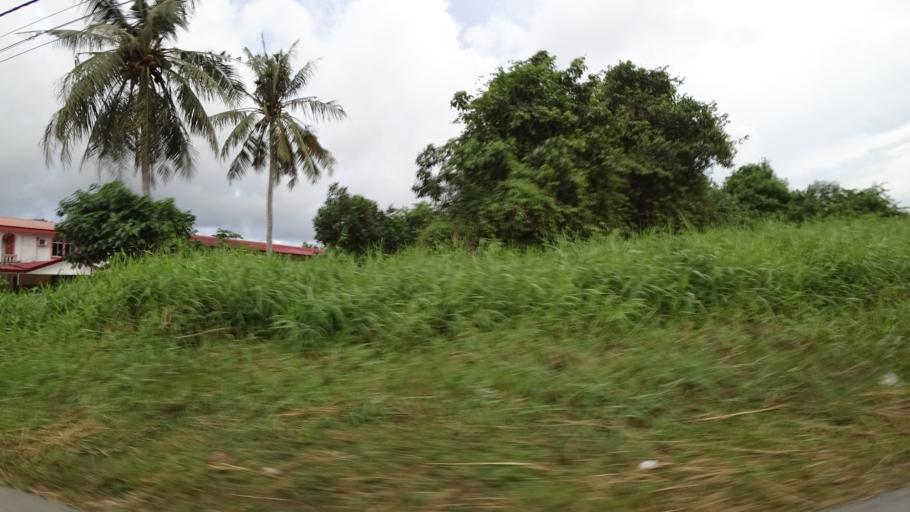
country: BN
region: Brunei and Muara
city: Bandar Seri Begawan
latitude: 4.8556
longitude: 114.8541
